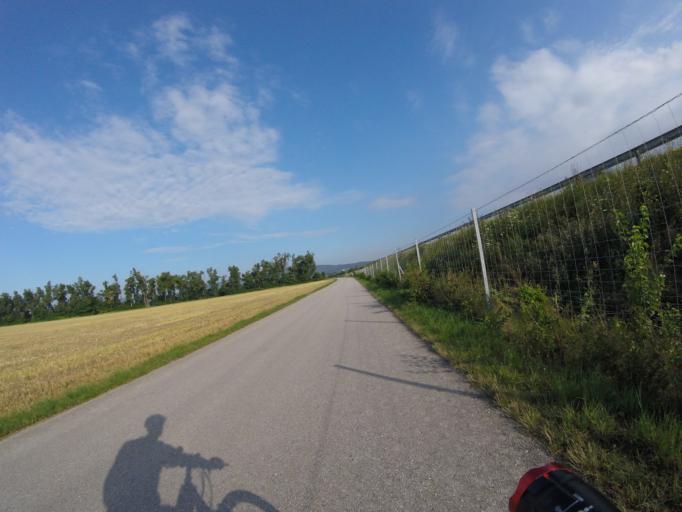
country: AT
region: Lower Austria
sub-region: Politischer Bezirk Baden
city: Trumau
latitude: 48.0249
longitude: 16.3493
